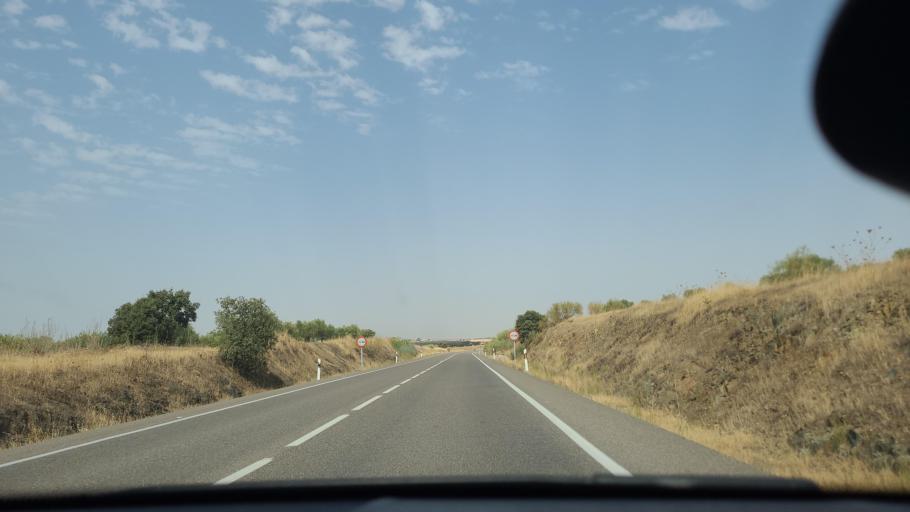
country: ES
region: Andalusia
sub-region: Province of Cordoba
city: Fuente Obejuna
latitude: 38.2650
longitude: -5.4974
